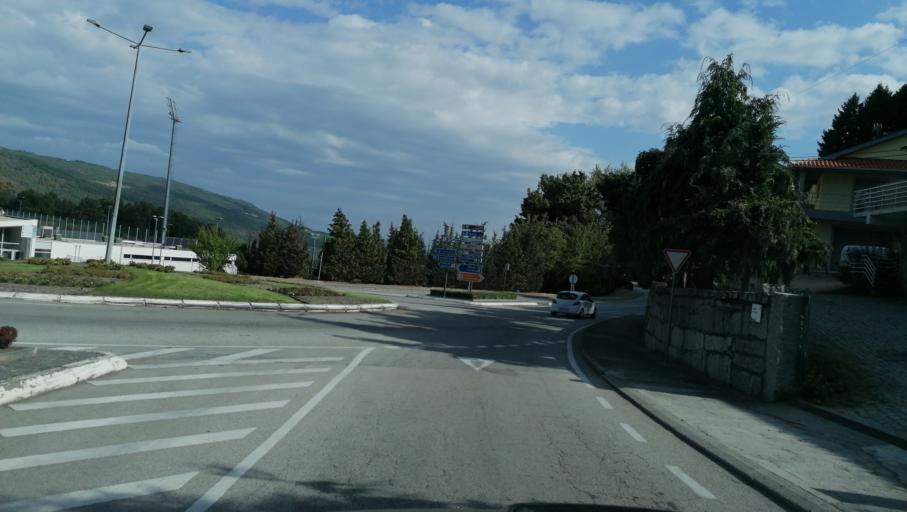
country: PT
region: Vila Real
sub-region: Vila Pouca de Aguiar
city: Vila Pouca de Aguiar
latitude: 41.5016
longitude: -7.6395
